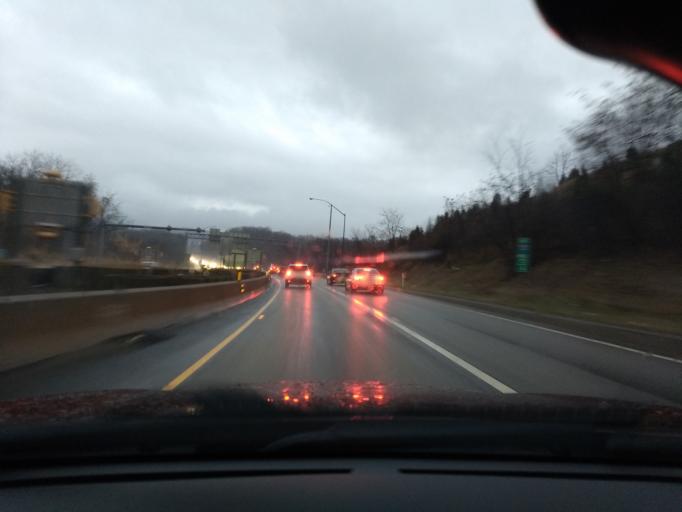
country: US
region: Pennsylvania
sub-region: Allegheny County
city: Homestead
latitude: 40.4249
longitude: -79.9096
